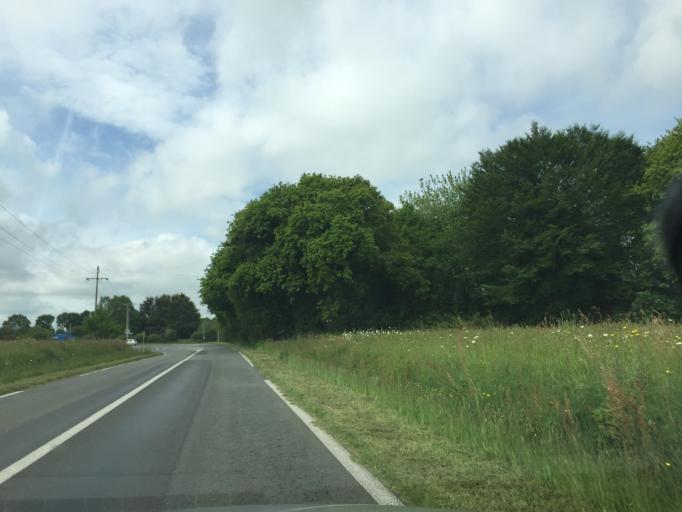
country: FR
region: Brittany
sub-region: Departement des Cotes-d'Armor
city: Saint-Cast-le-Guildo
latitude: 48.5980
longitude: -2.2481
